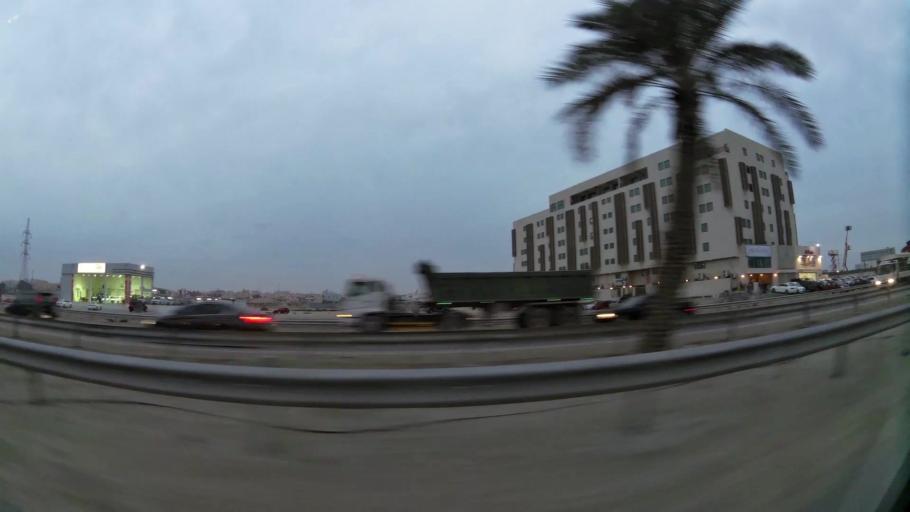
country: BH
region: Northern
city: Ar Rifa'
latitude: 26.1482
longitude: 50.5762
